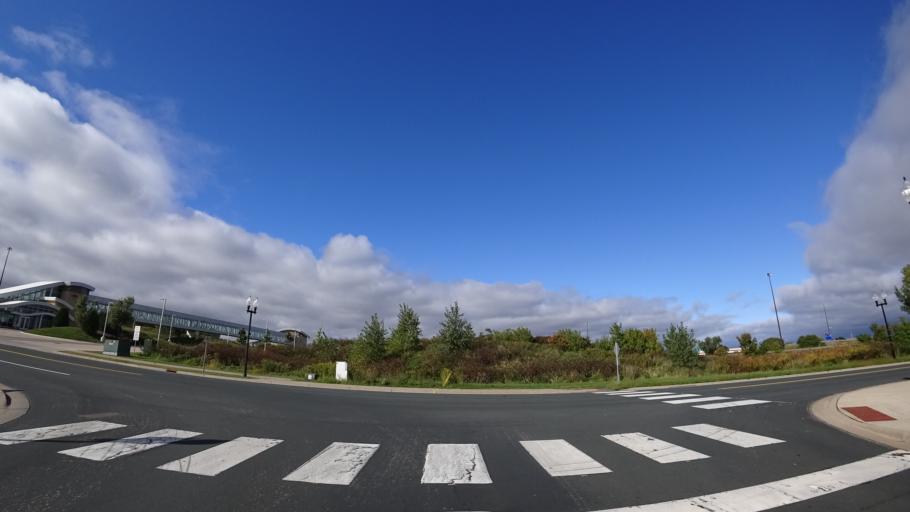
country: US
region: Minnesota
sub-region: Dakota County
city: Eagan
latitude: 44.8134
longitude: -93.2175
